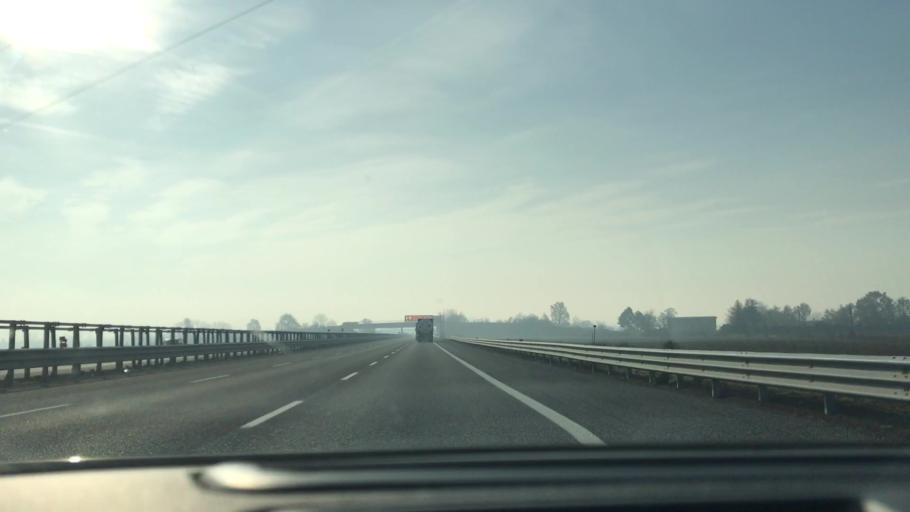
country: IT
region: Piedmont
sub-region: Provincia di Alessandria
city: Alessandria
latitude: 44.8920
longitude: 8.5687
